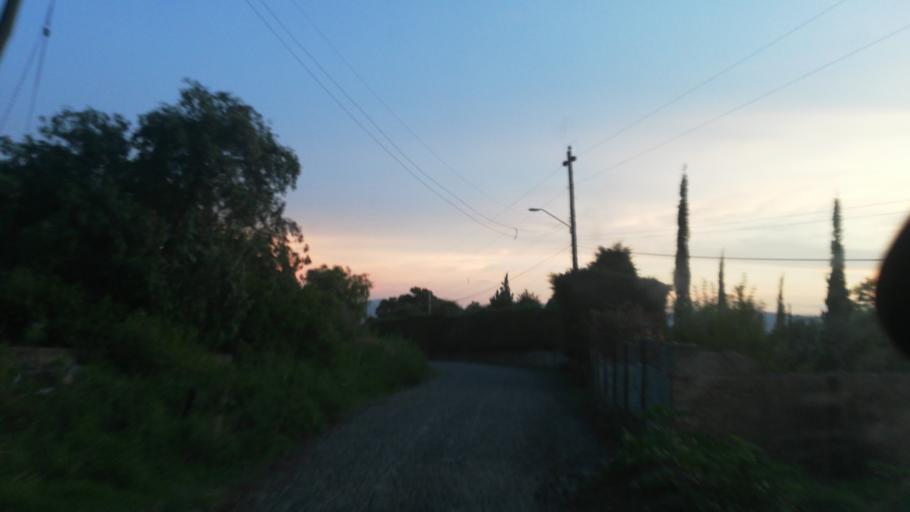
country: BO
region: Cochabamba
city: Cochabamba
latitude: -17.3237
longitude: -66.2084
